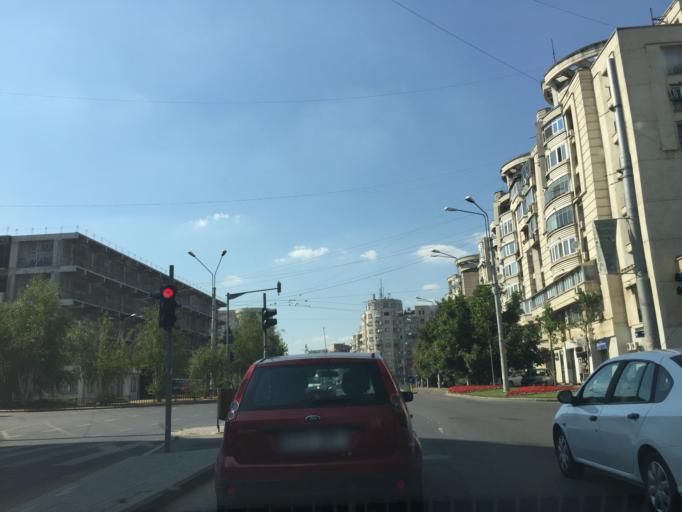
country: RO
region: Bucuresti
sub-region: Municipiul Bucuresti
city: Bucharest
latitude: 44.4287
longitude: 26.1084
